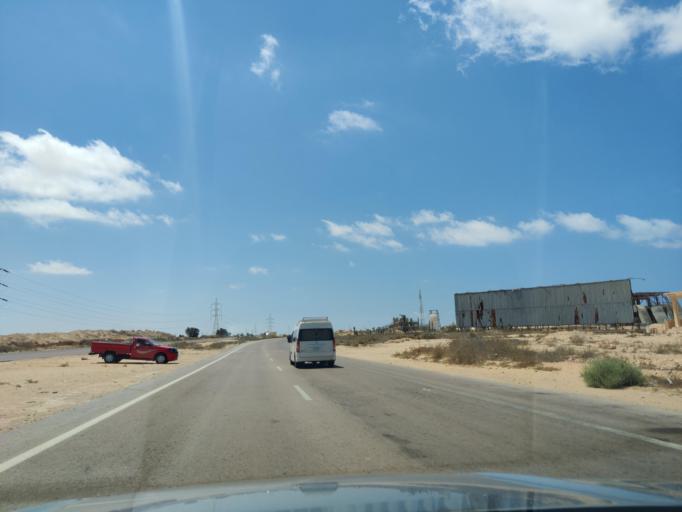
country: EG
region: Muhafazat Matruh
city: Al `Alamayn
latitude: 31.0597
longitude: 28.2072
